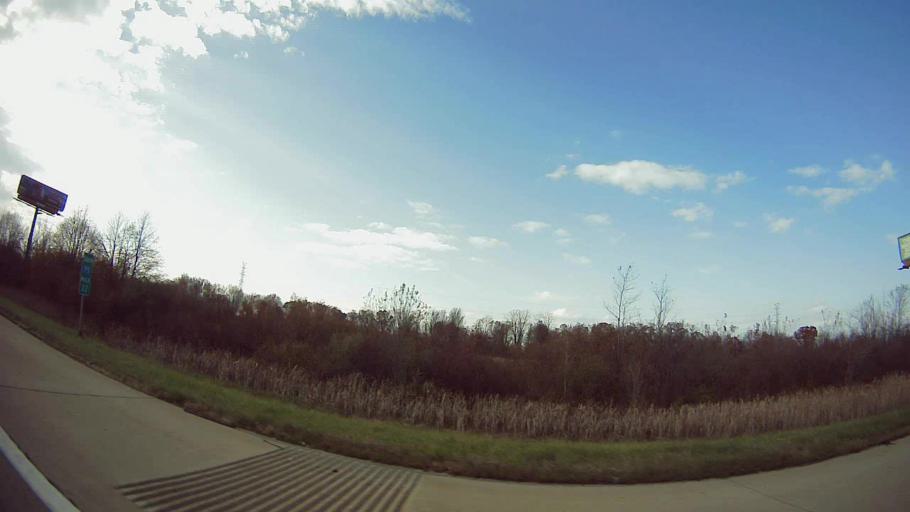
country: US
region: Michigan
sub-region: Monroe County
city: South Rockwood
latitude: 42.0126
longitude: -83.3078
